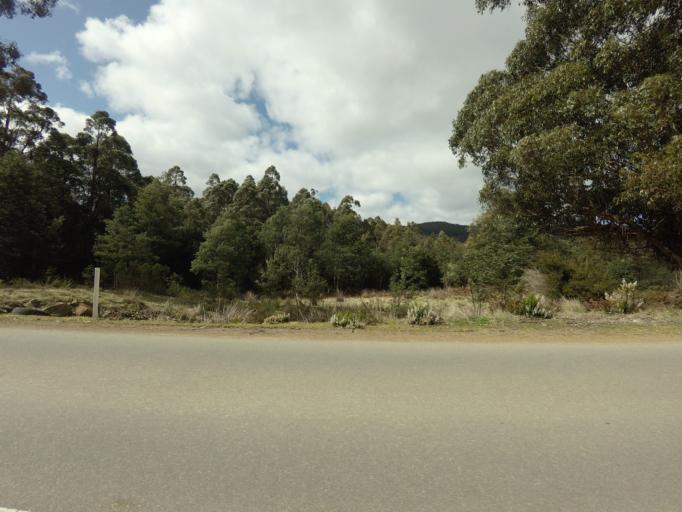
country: AU
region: Tasmania
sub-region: Huon Valley
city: Geeveston
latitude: -43.3589
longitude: 146.9593
